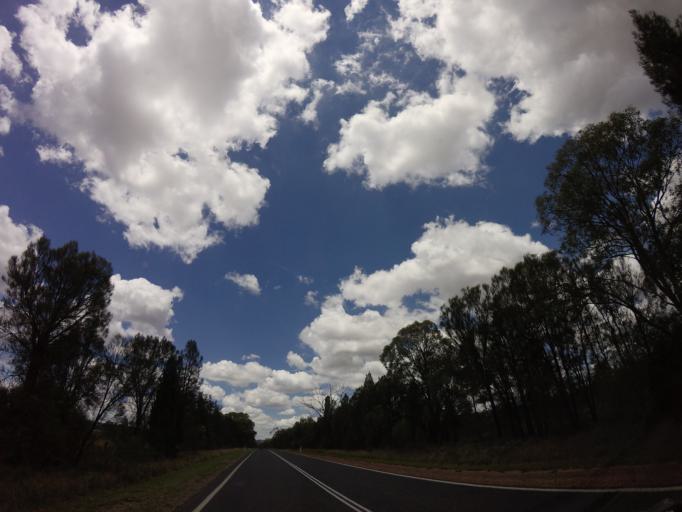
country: AU
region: Queensland
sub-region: Western Downs
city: Dalby
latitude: -27.9640
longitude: 151.1177
